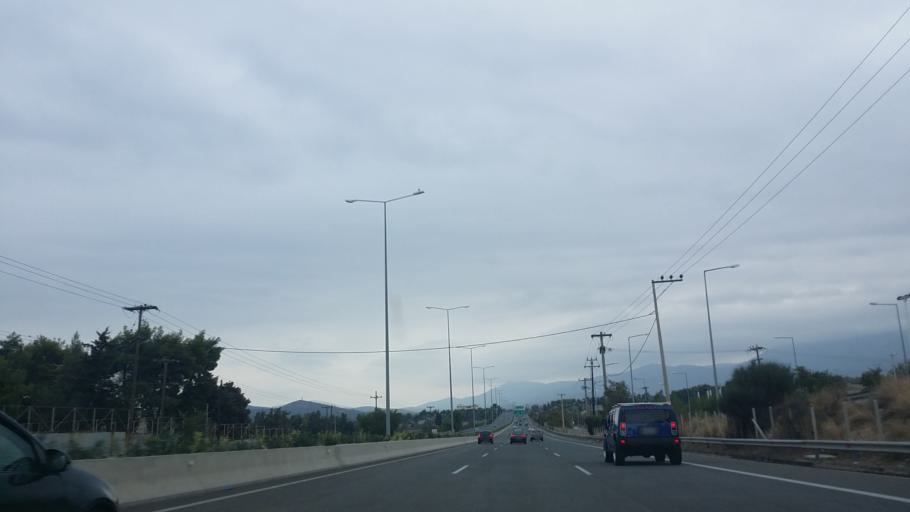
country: GR
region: Central Greece
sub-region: Nomos Voiotias
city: Oinofyta
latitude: 38.3011
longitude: 23.6573
